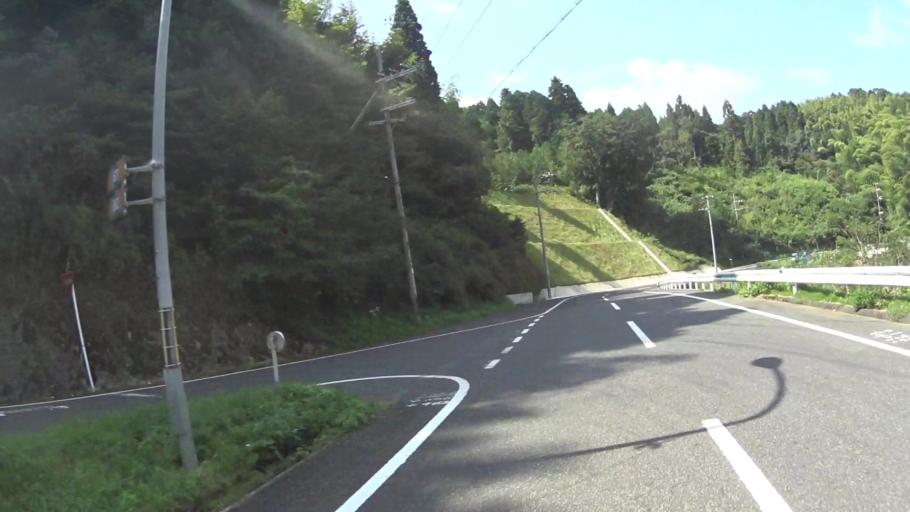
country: JP
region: Kyoto
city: Miyazu
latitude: 35.6880
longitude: 135.2539
